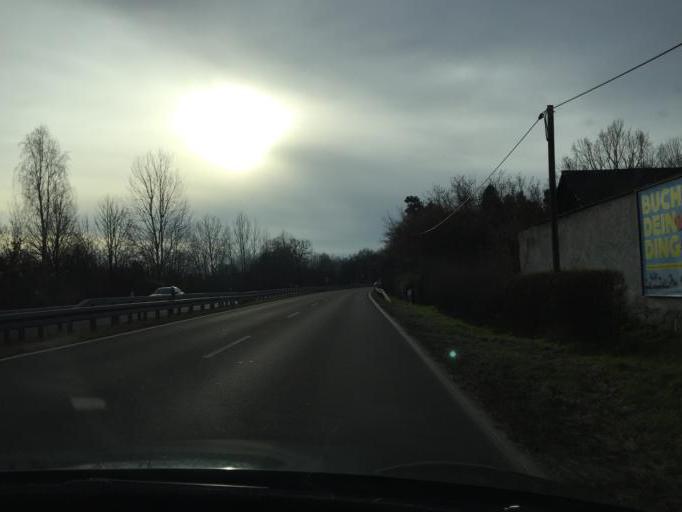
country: DE
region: Brandenburg
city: Peitz
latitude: 51.7989
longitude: 14.3814
